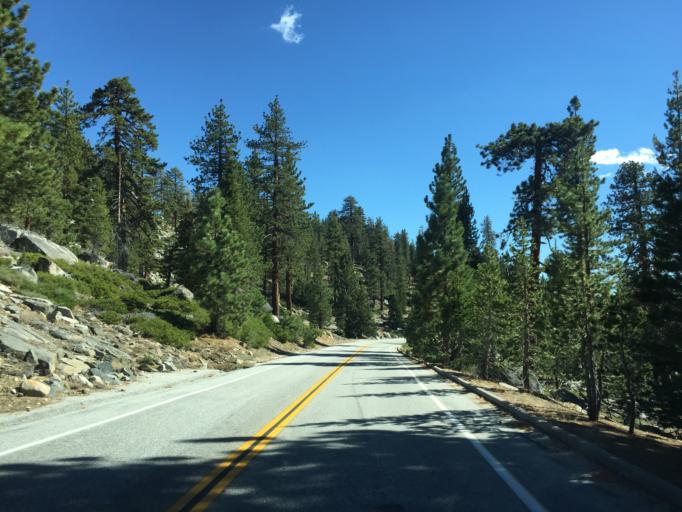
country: US
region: California
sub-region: Mariposa County
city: Yosemite Valley
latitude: 37.8473
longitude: -119.5958
